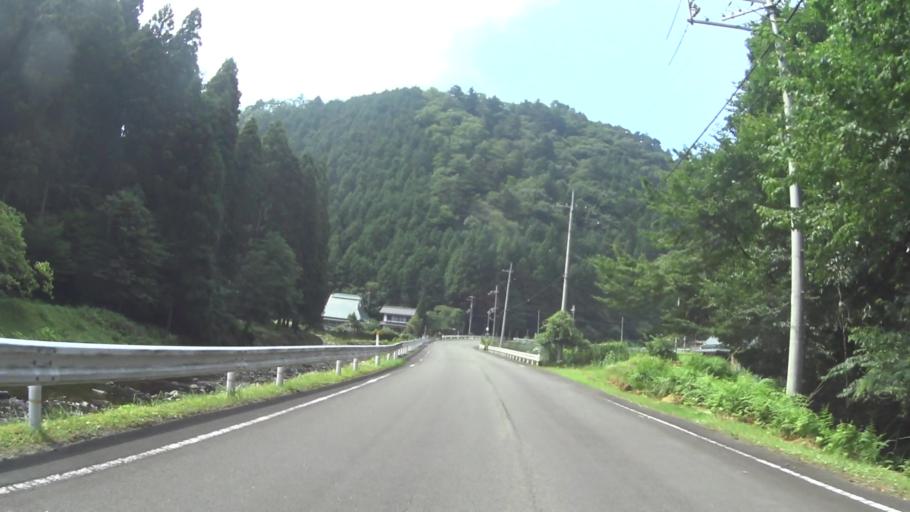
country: JP
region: Fukui
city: Obama
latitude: 35.3418
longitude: 135.6473
